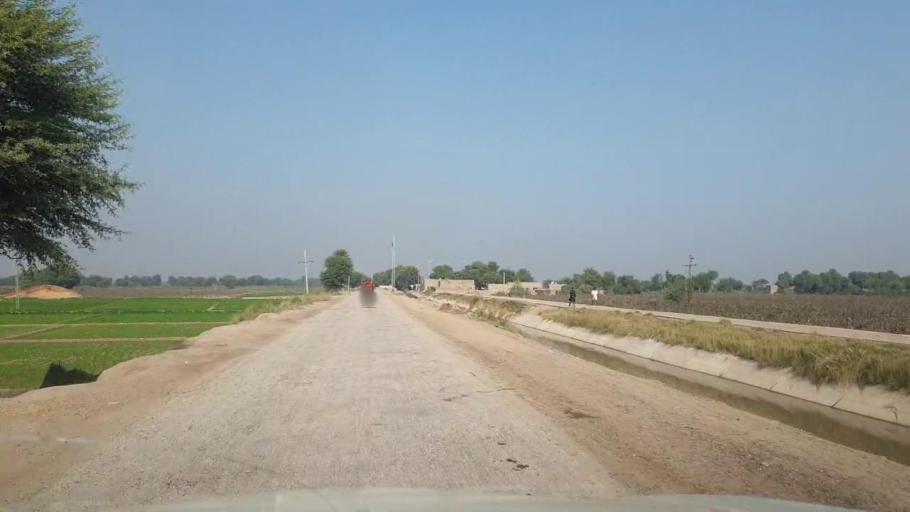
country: PK
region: Sindh
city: Bhan
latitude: 26.5402
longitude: 67.7748
